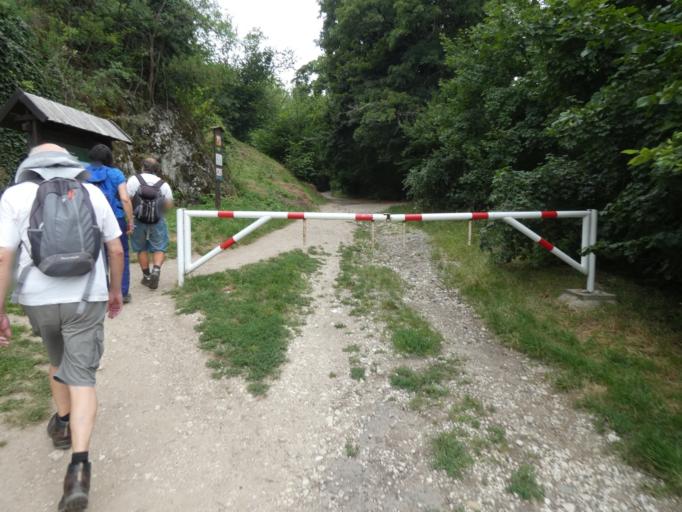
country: CZ
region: South Moravian
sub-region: Okres Breclav
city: Mikulov
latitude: 48.8427
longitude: 16.6412
